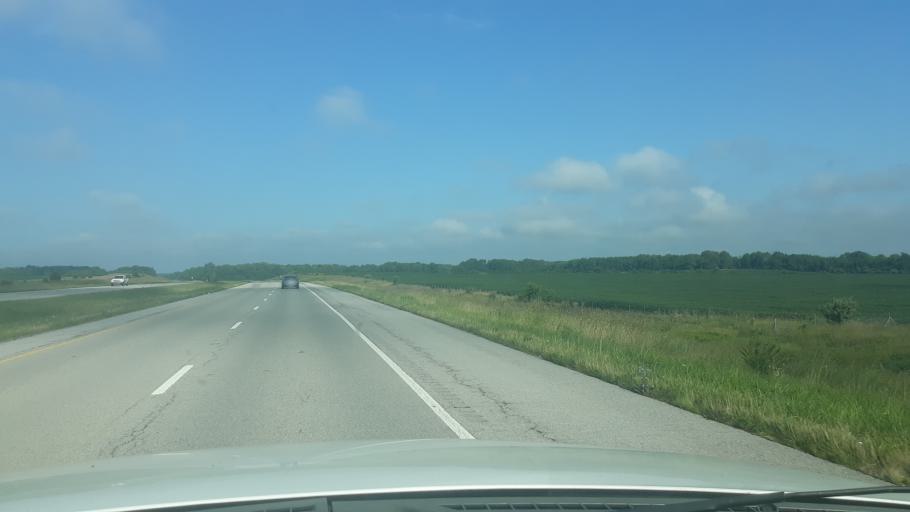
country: US
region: Illinois
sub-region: Saline County
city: Carrier Mills
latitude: 37.7325
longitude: -88.6123
